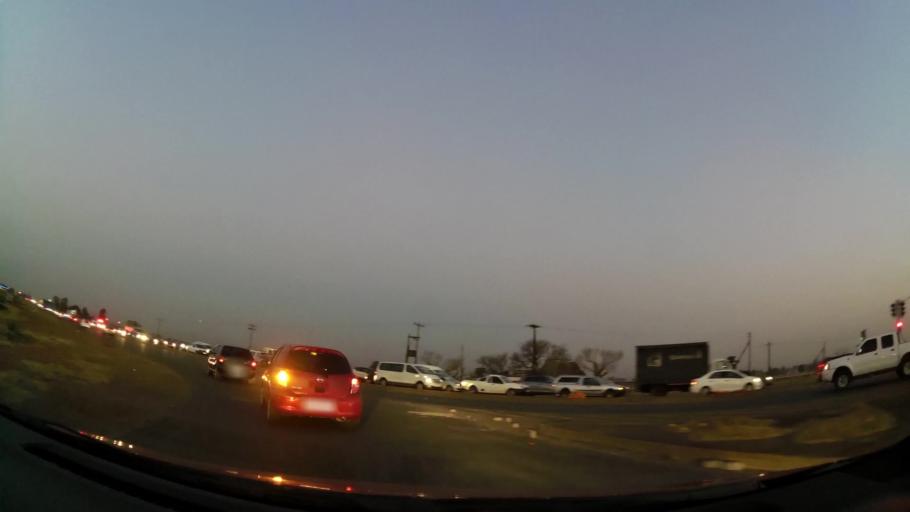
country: ZA
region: Gauteng
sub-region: City of Johannesburg Metropolitan Municipality
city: Soweto
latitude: -26.2990
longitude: 27.8160
